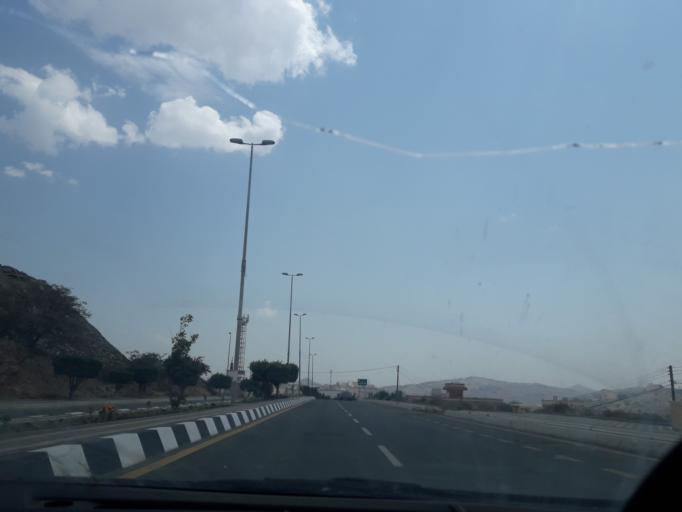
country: SA
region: Mintaqat al Bahah
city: Al Bahah
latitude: 20.0069
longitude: 41.4813
